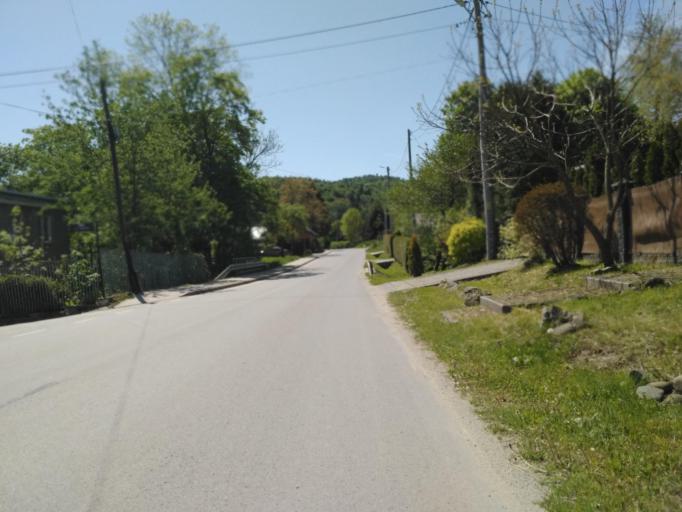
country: PL
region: Subcarpathian Voivodeship
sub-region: Powiat krosnienski
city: Iwonicz-Zdroj
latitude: 49.5705
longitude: 21.7927
